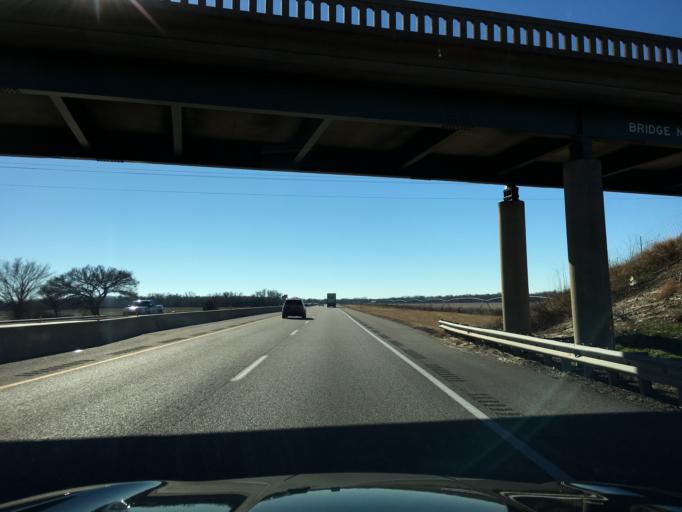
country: US
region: Kansas
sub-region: Sumner County
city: Belle Plaine
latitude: 37.4070
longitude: -97.3237
